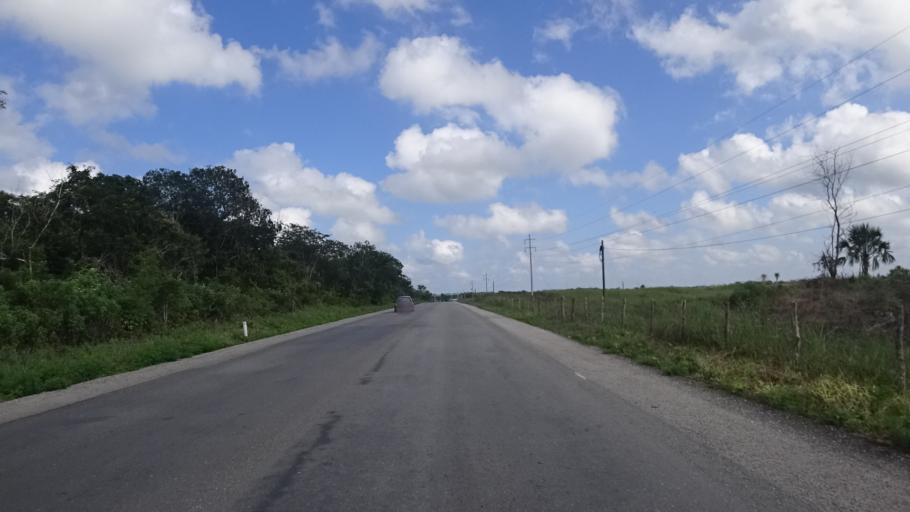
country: MX
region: Yucatan
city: Espita
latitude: 21.0028
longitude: -88.1764
